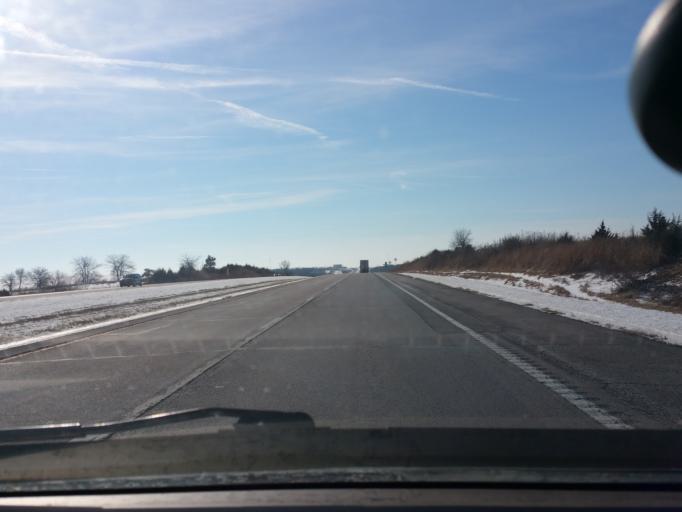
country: US
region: Iowa
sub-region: Decatur County
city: Lamoni
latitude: 40.4925
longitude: -93.9698
